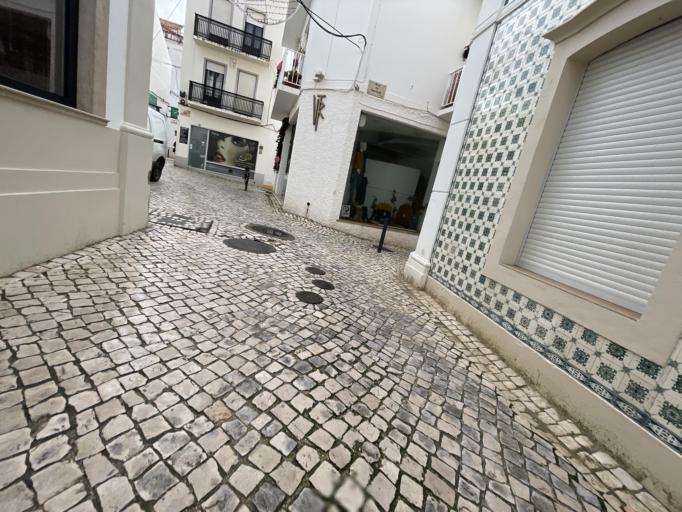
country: PT
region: Leiria
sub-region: Nazare
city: Nazare
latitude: 39.6013
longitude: -9.0712
